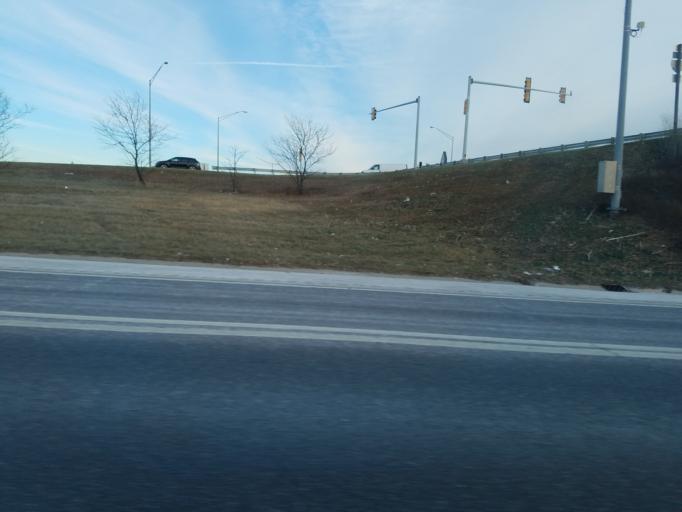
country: US
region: Illinois
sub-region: DuPage County
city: Woodridge
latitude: 41.7257
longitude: -88.0344
